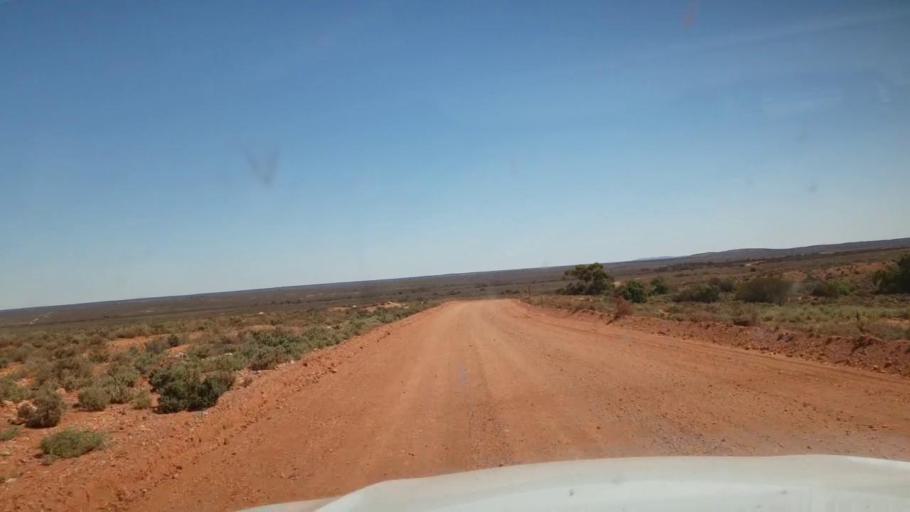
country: AU
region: South Australia
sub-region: Whyalla
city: Whyalla
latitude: -32.6852
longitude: 137.1227
